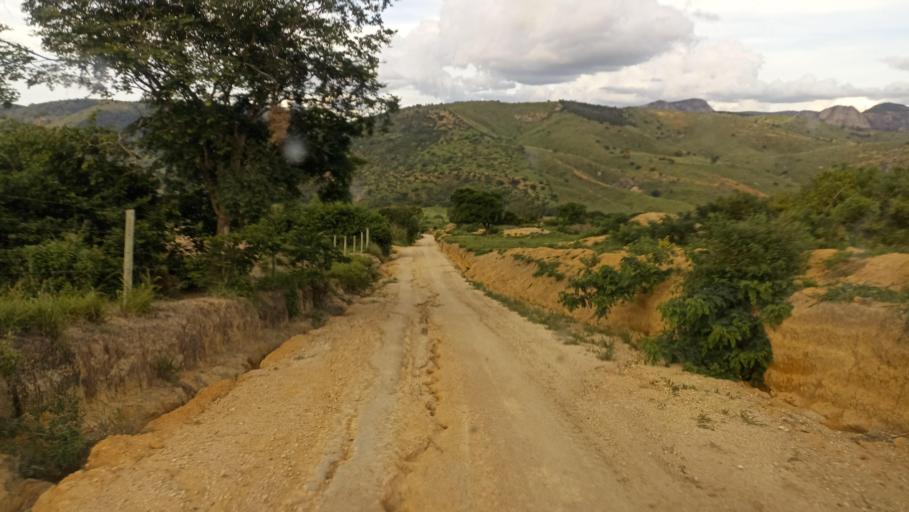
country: BR
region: Minas Gerais
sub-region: Almenara
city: Almenara
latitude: -16.5429
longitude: -40.4471
